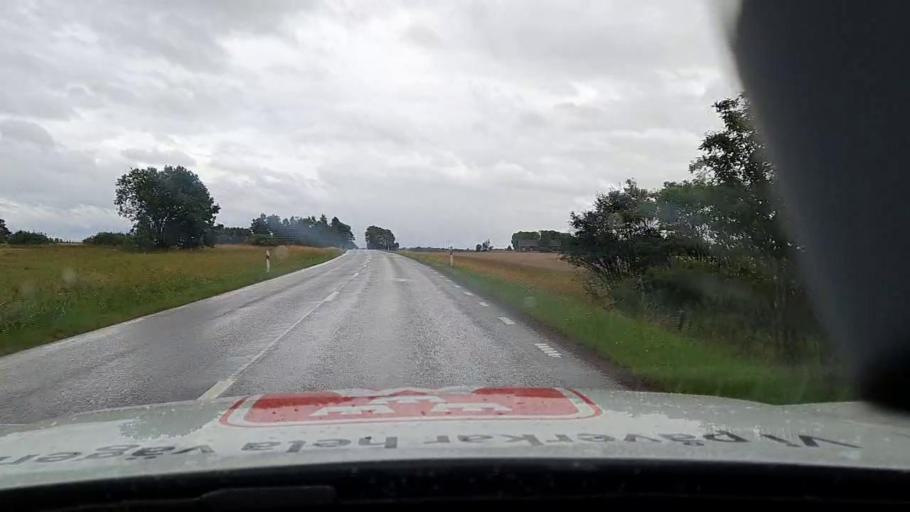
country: SE
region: Vaestra Goetaland
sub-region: Toreboda Kommun
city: Toereboda
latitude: 58.6045
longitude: 14.0096
